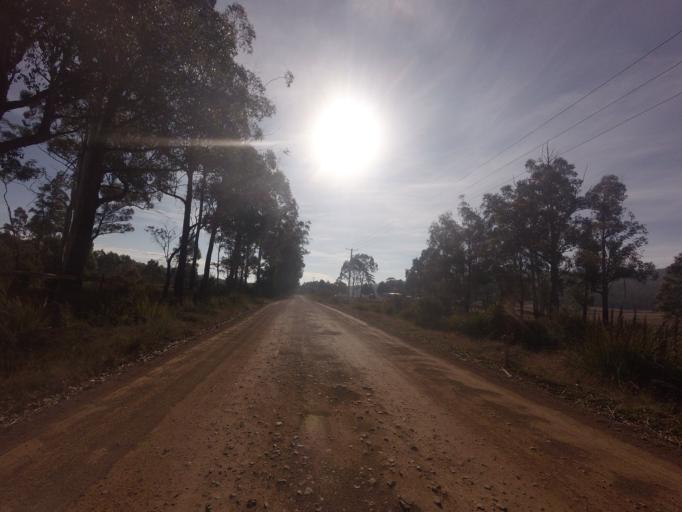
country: AU
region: Tasmania
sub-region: Sorell
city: Sorell
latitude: -42.4929
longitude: 147.5250
